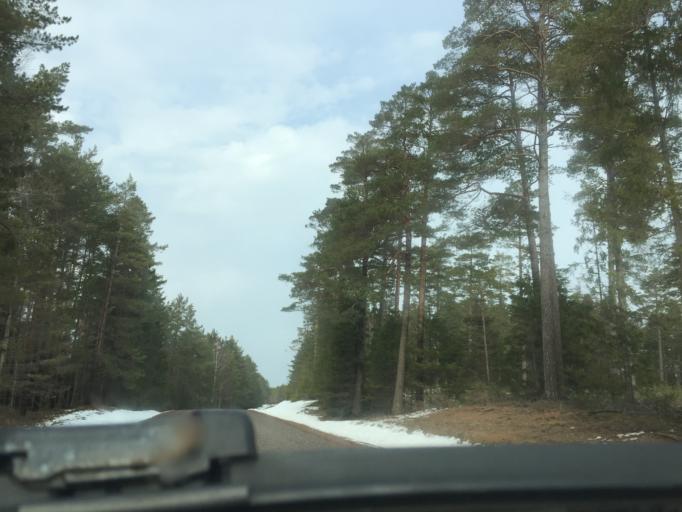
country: EE
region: Saare
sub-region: Kuressaare linn
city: Kuressaare
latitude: 58.4034
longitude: 22.1739
